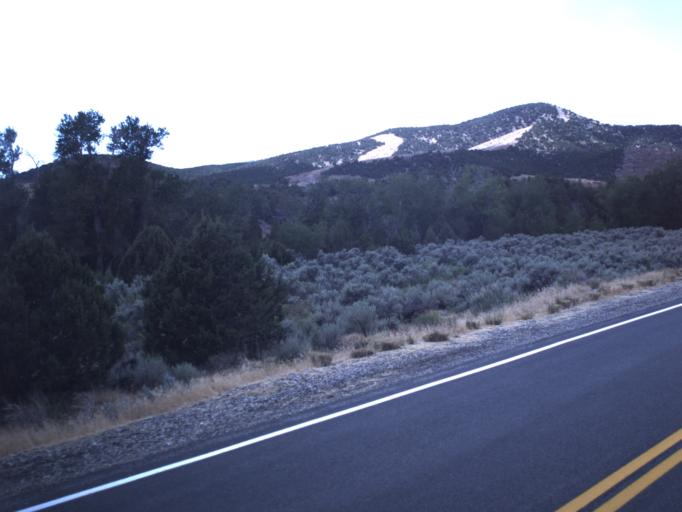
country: US
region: Utah
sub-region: Tooele County
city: Grantsville
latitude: 40.3345
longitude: -112.5258
